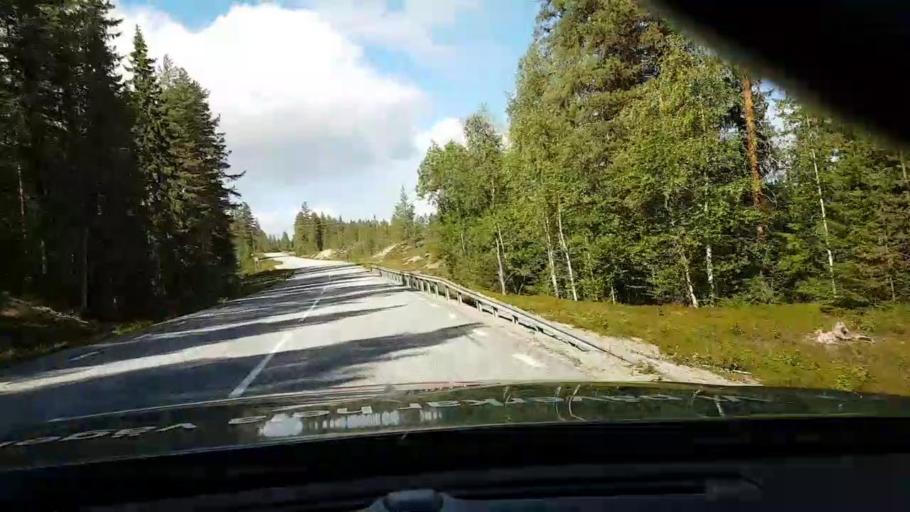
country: SE
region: Vaesternorrland
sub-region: OErnskoeldsviks Kommun
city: Bredbyn
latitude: 63.6677
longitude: 17.8298
